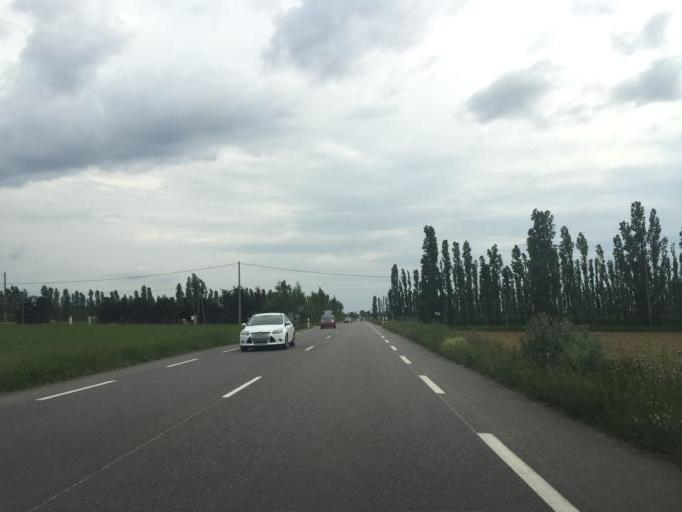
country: FR
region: Rhone-Alpes
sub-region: Departement de la Drome
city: Alixan
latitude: 44.9977
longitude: 5.0342
